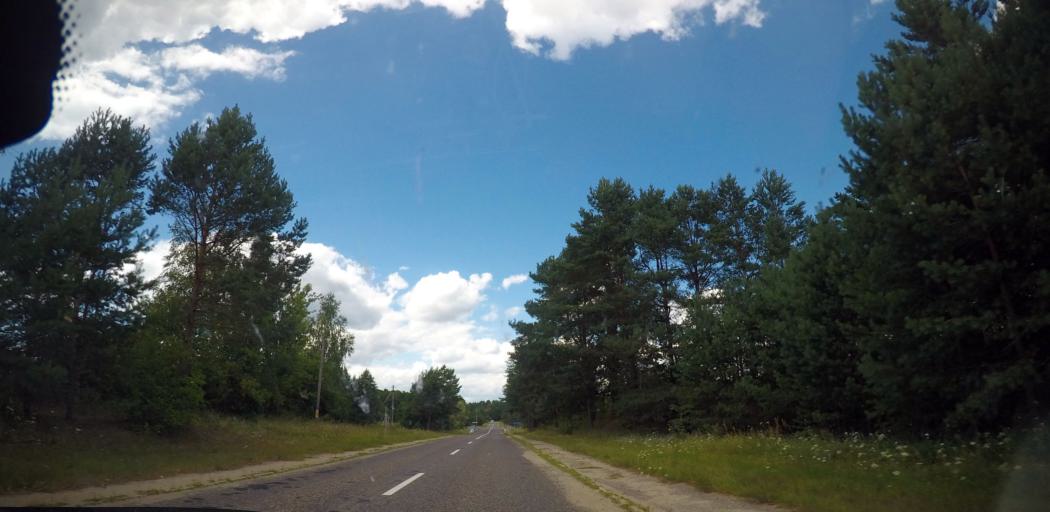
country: BY
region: Grodnenskaya
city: Skidal'
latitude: 53.8189
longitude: 24.2438
